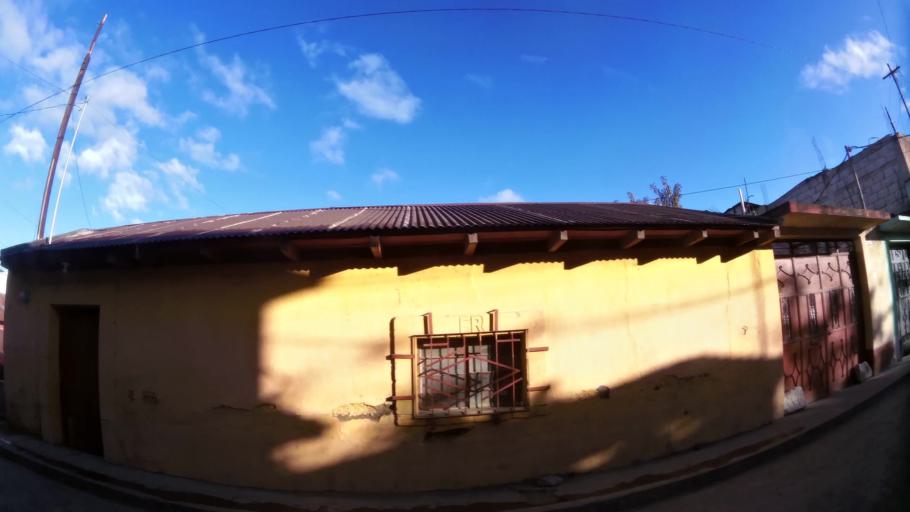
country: GT
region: Quetzaltenango
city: Quetzaltenango
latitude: 14.8326
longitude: -91.5242
